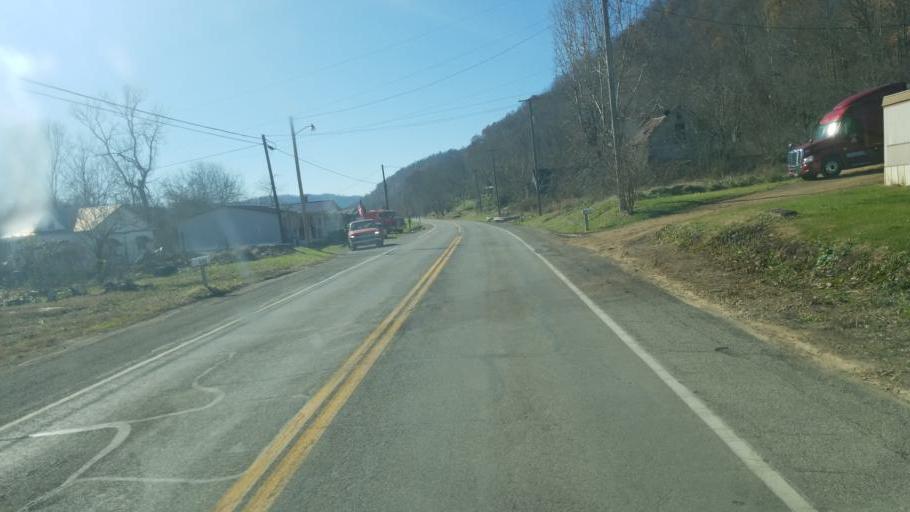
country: US
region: Kentucky
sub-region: Lewis County
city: Vanceburg
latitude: 38.6270
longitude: -83.2611
